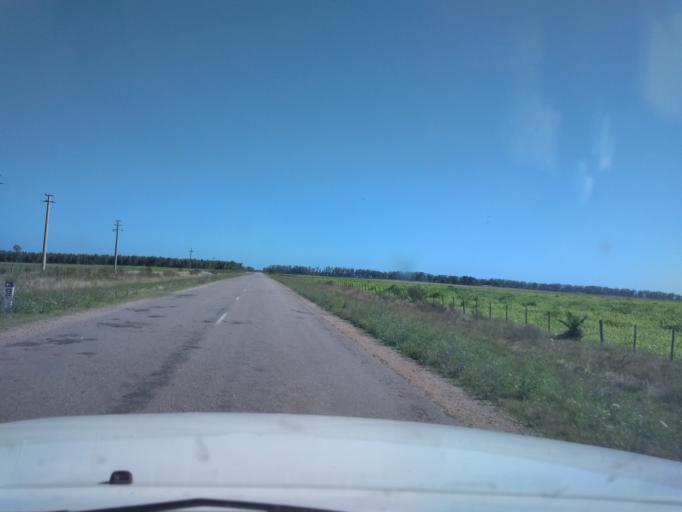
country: UY
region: Canelones
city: San Ramon
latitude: -34.1534
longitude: -55.9463
